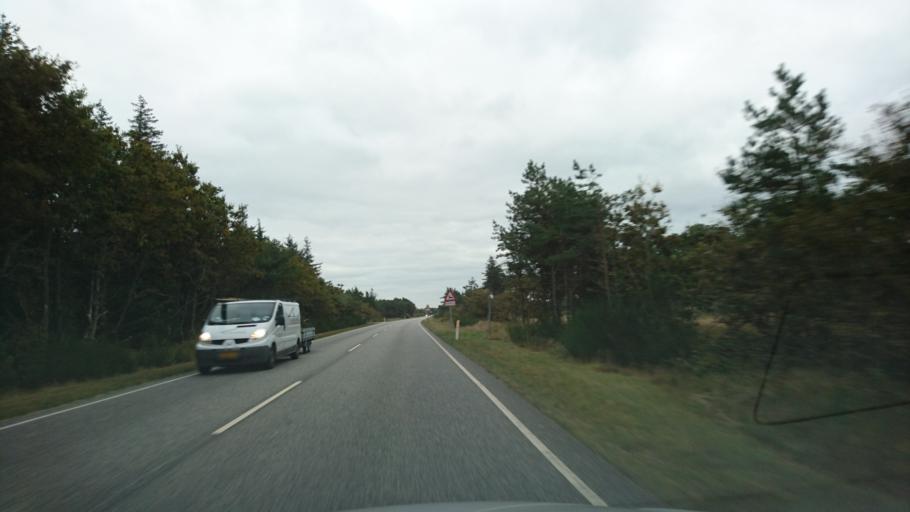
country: DK
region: North Denmark
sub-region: Frederikshavn Kommune
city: Skagen
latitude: 57.6998
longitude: 10.4877
